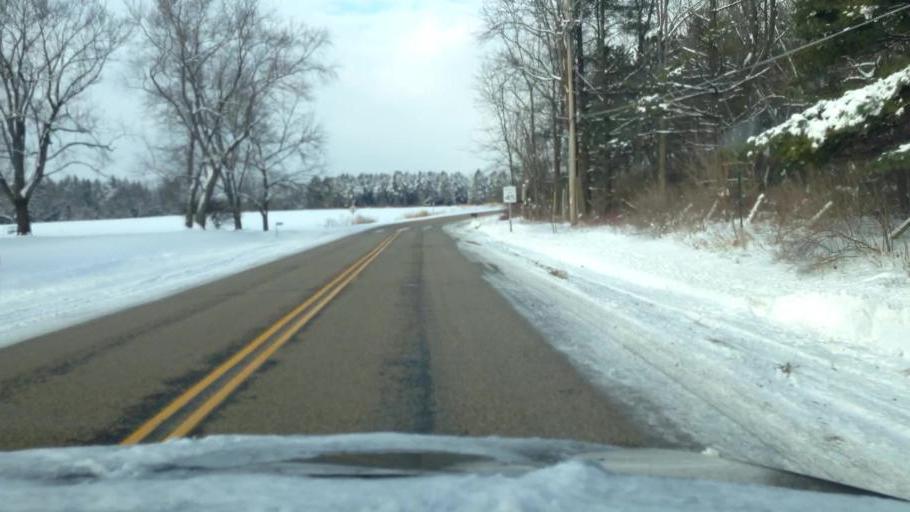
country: US
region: Wisconsin
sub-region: Walworth County
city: East Troy
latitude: 42.8292
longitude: -88.4244
